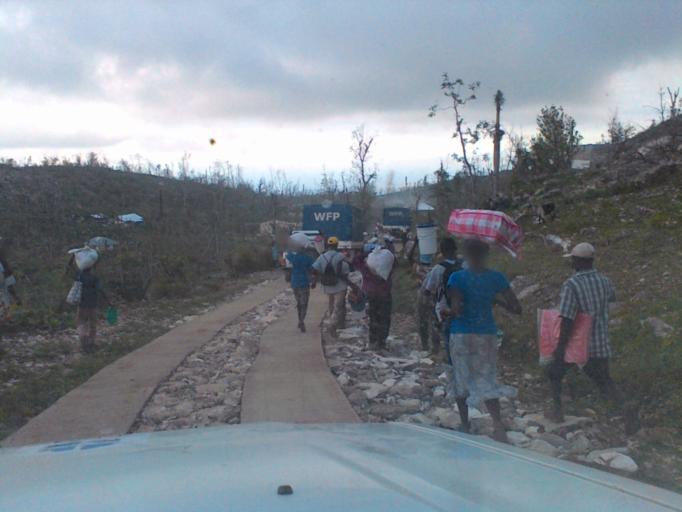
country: HT
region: Grandans
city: Moron
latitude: 18.4871
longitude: -74.1130
